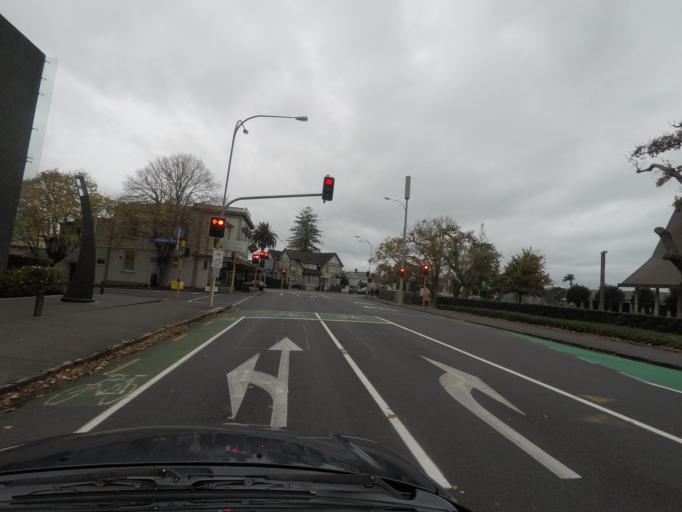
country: NZ
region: Auckland
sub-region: Auckland
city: Auckland
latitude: -36.8596
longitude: 174.7828
